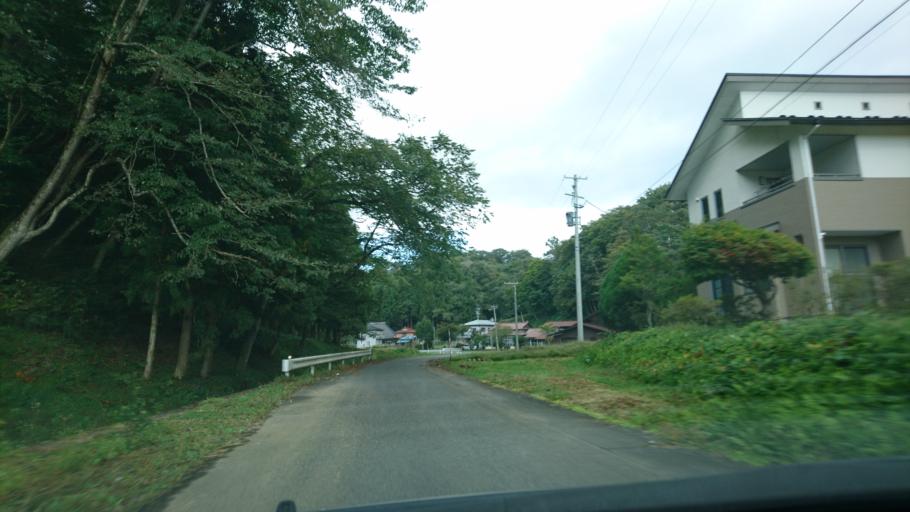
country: JP
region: Iwate
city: Ichinoseki
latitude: 38.8957
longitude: 141.0898
